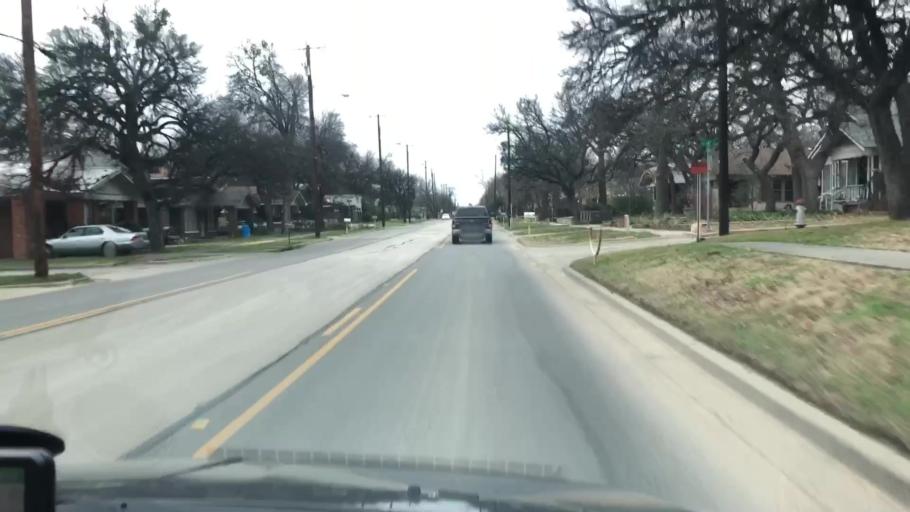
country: US
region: Texas
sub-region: Palo Pinto County
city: Mineral Wells
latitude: 32.8193
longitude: -98.1128
